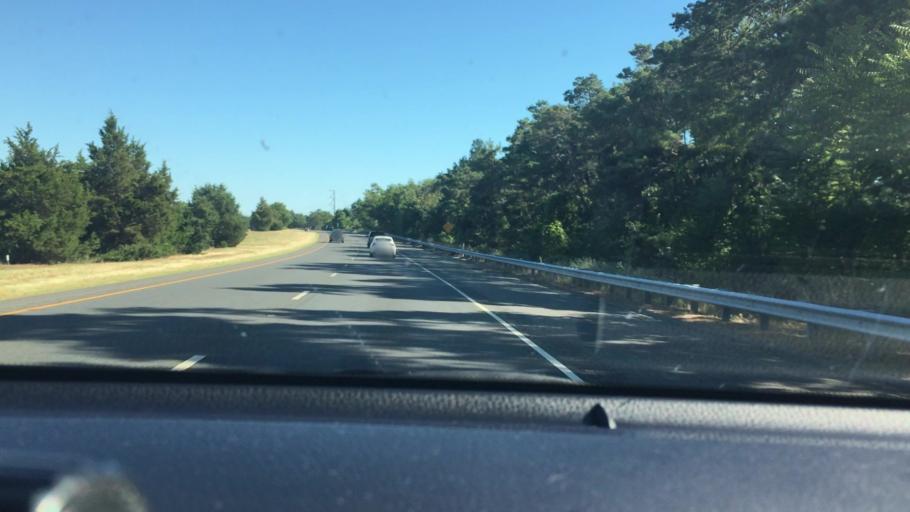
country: US
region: New Jersey
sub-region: Cumberland County
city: South Vineland
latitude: 39.4668
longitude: -75.0746
